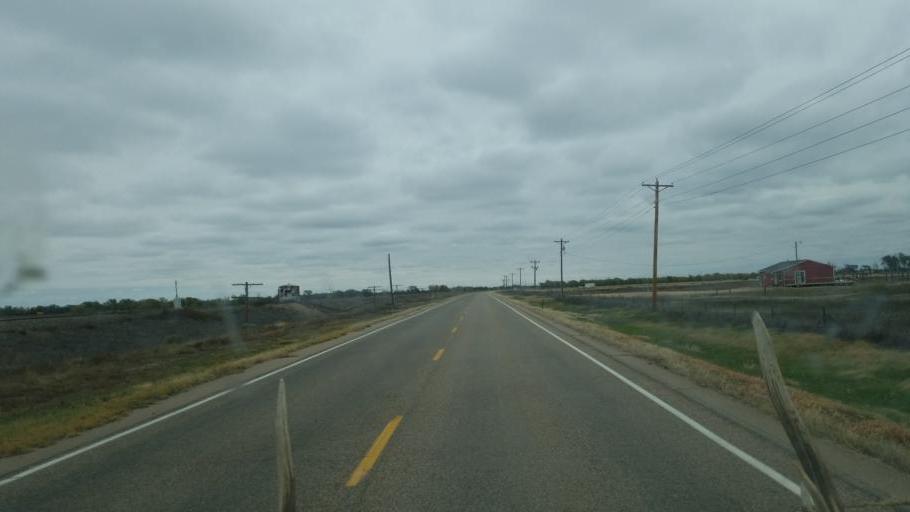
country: US
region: Colorado
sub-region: Crowley County
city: Ordway
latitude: 38.1999
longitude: -103.8295
